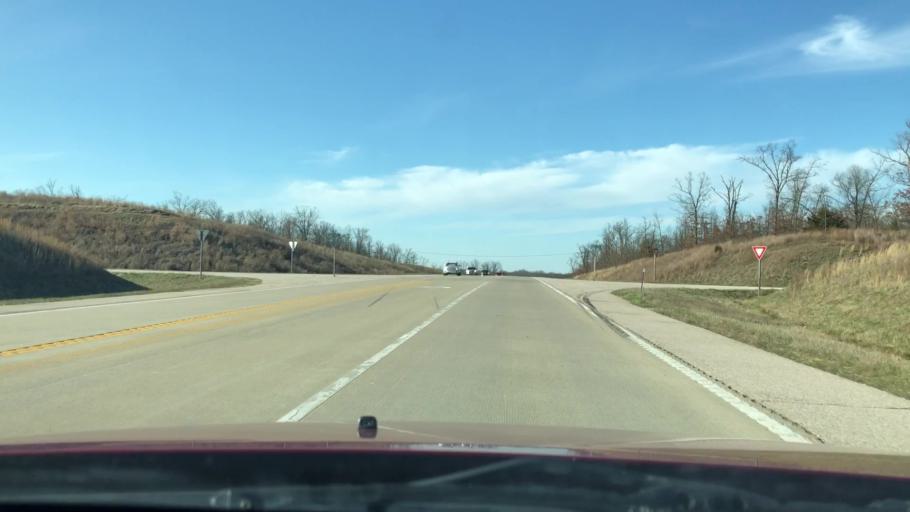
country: US
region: Missouri
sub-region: Camden County
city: Camdenton
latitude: 37.9350
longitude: -92.7149
